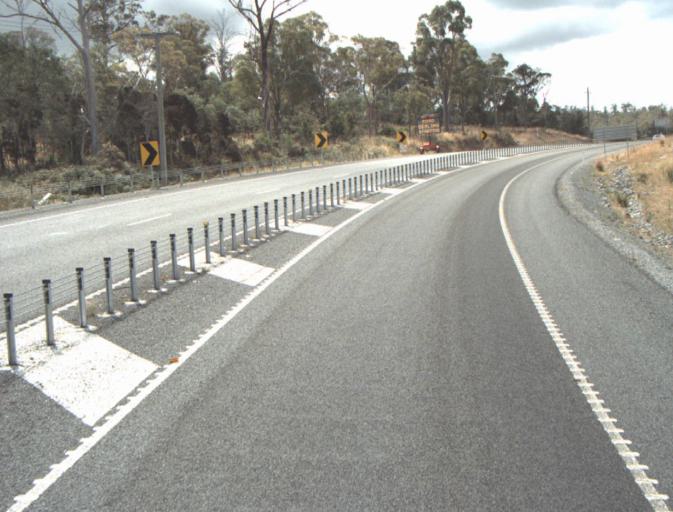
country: AU
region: Tasmania
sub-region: Launceston
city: Mayfield
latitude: -41.2996
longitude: 147.0494
